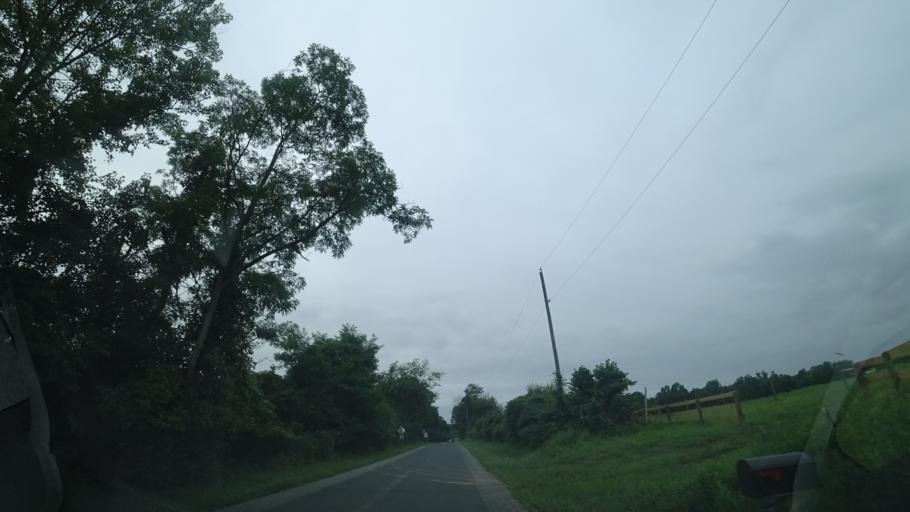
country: US
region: Maryland
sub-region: Montgomery County
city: Poolesville
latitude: 39.1129
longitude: -77.4475
